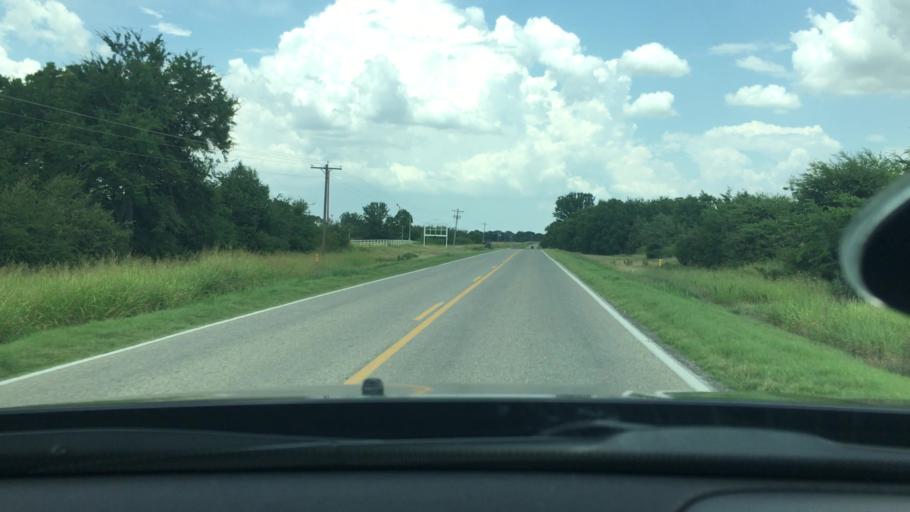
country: US
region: Oklahoma
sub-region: Marshall County
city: Oakland
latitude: 34.0123
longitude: -96.8789
